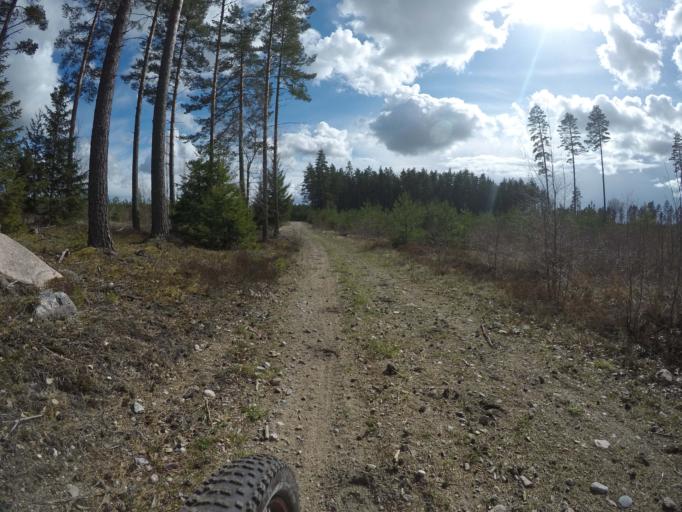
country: SE
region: Vaestmanland
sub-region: Kungsors Kommun
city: Kungsoer
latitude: 59.3472
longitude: 16.1077
